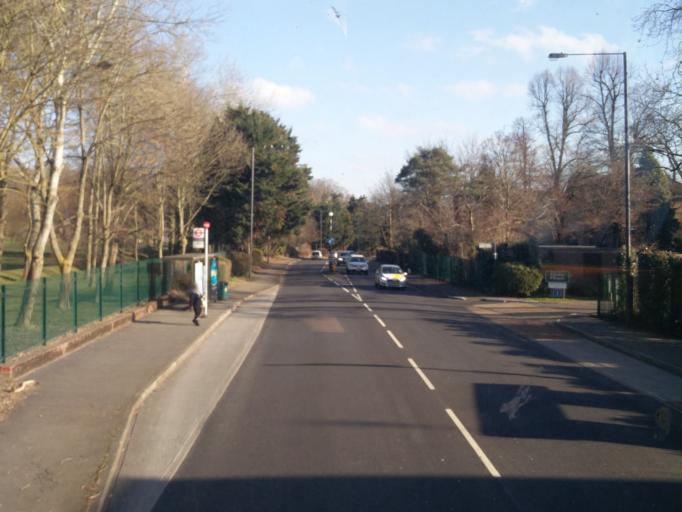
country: GB
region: England
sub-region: Greater London
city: Pinner
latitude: 51.6000
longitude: -0.3911
